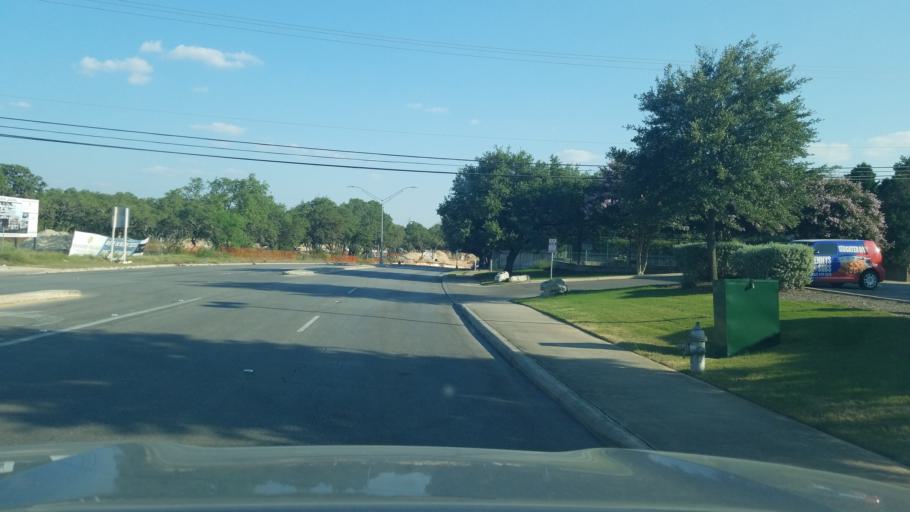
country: US
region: Texas
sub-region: Bexar County
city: Shavano Park
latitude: 29.6020
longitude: -98.5331
